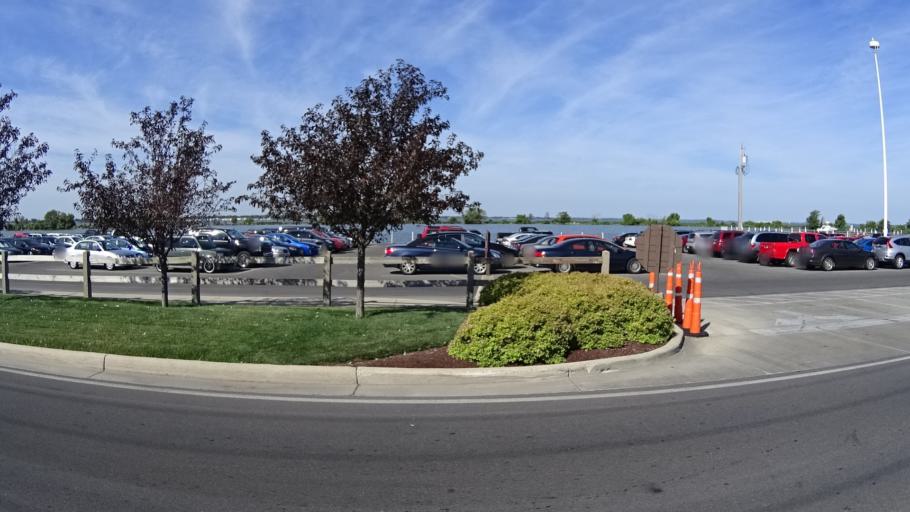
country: US
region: Ohio
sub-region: Erie County
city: Sandusky
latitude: 41.4748
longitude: -82.6794
